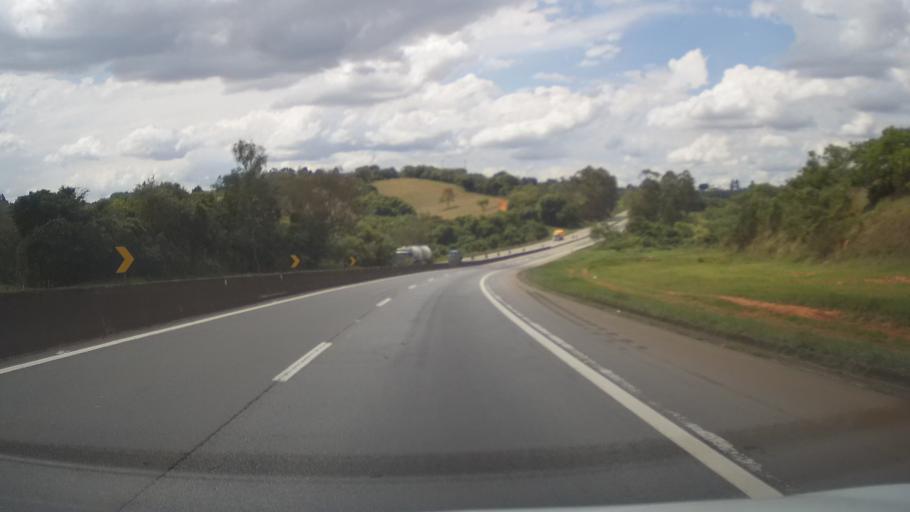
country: BR
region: Minas Gerais
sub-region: Nepomuceno
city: Nepomuceno
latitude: -21.2608
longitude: -45.1397
